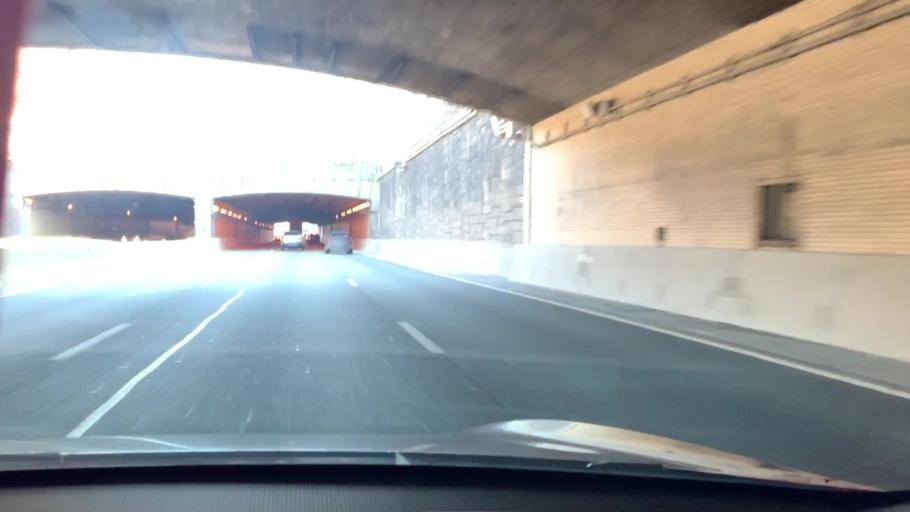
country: US
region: New York
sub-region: Bronx
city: The Bronx
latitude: 40.8339
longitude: -73.8627
